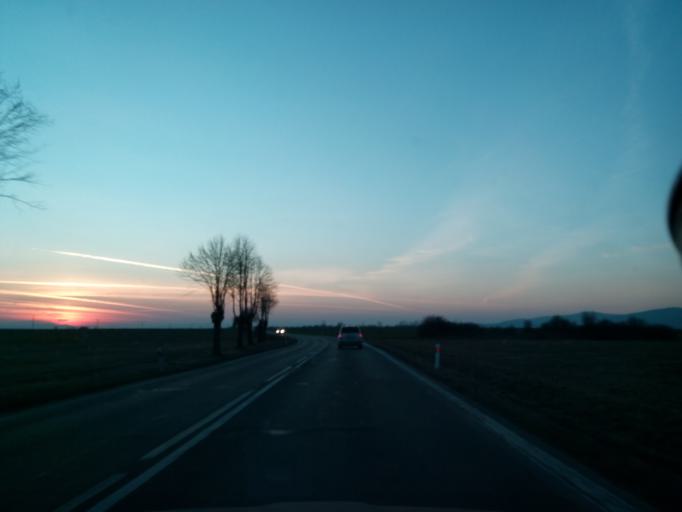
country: SK
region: Kosicky
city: Sobrance
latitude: 48.7639
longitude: 22.1068
